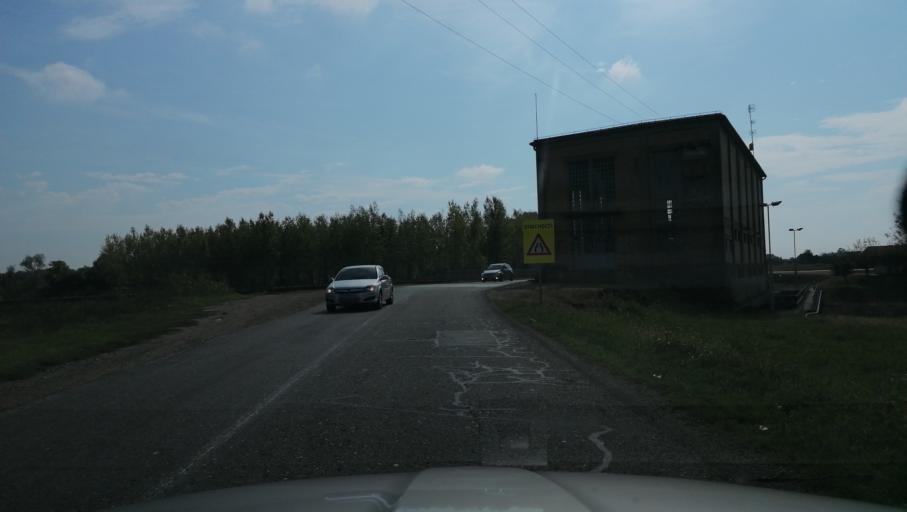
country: RS
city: Bosut
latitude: 44.9441
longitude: 19.3682
